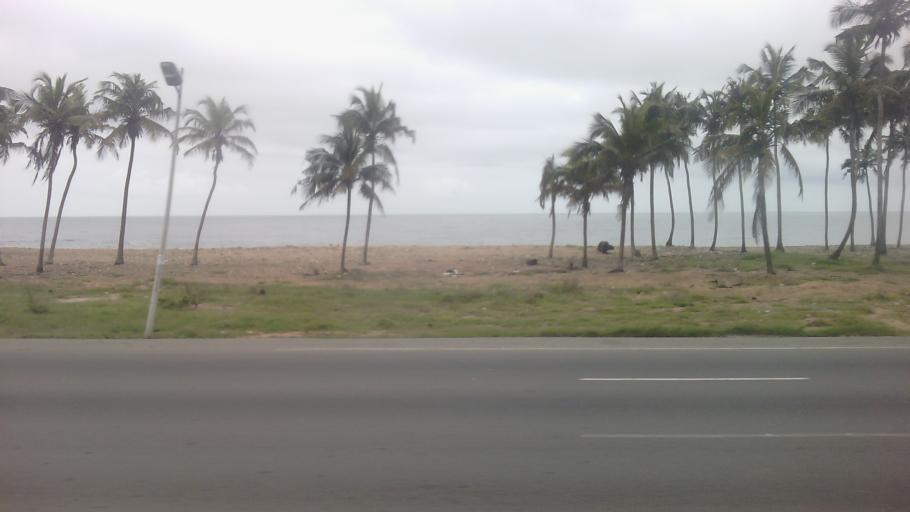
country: CI
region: Lagunes
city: Abidjan
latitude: 5.2456
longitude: -3.9357
